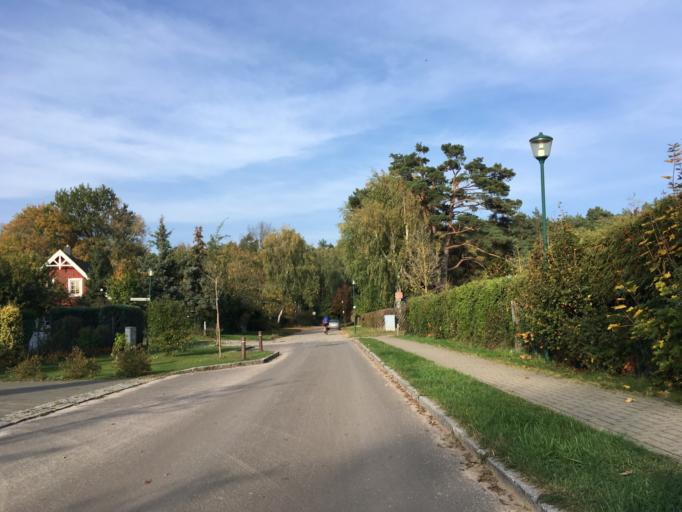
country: DE
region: Brandenburg
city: Glienicke
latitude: 52.6724
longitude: 13.3368
